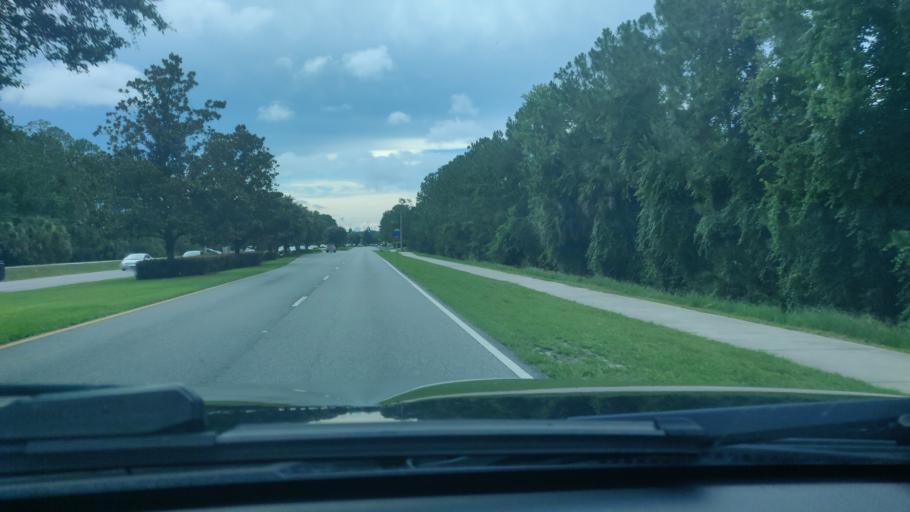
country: US
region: Florida
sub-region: Flagler County
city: Palm Coast
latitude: 29.5446
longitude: -81.2315
